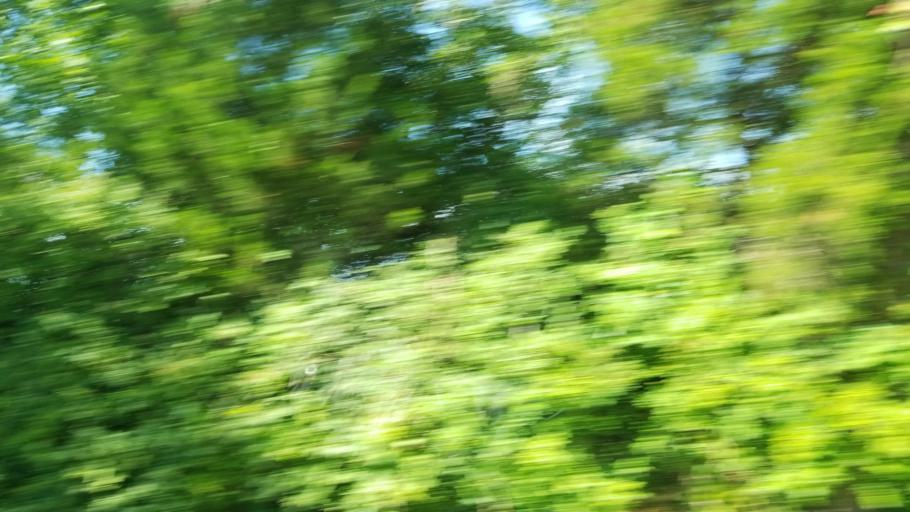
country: US
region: Illinois
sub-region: Williamson County
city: Marion
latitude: 37.7446
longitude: -88.8913
